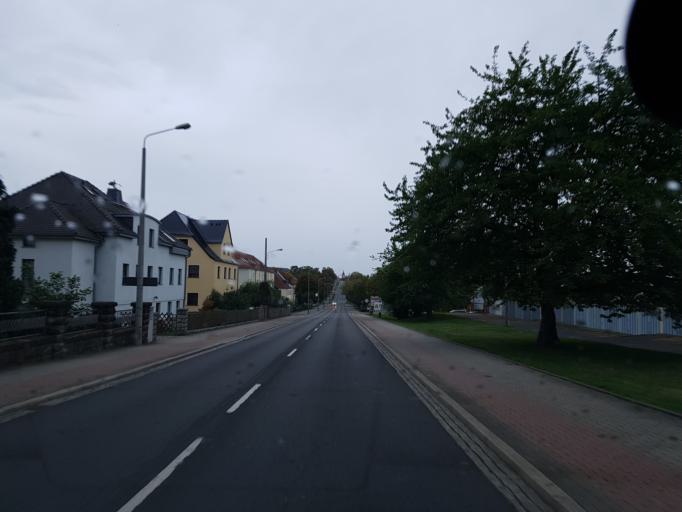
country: DE
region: Saxony
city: Riesa
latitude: 51.2994
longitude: 13.3011
